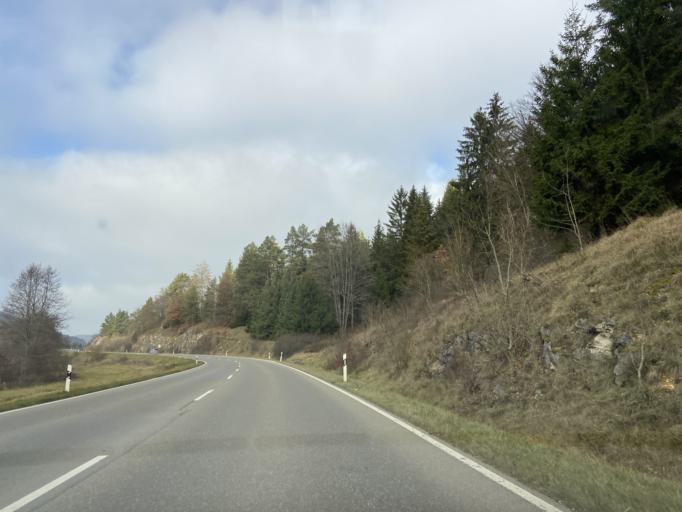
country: DE
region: Baden-Wuerttemberg
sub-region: Tuebingen Region
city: Neufra
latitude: 48.2583
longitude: 9.1741
